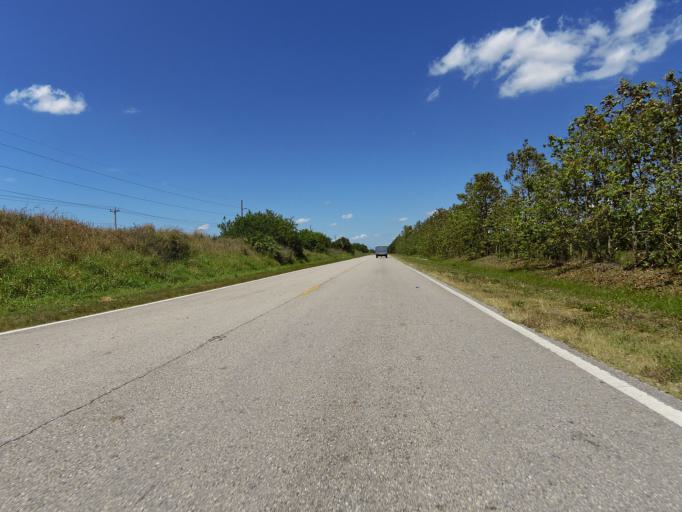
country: US
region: Florida
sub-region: Collier County
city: Immokalee
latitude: 26.3285
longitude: -81.4166
